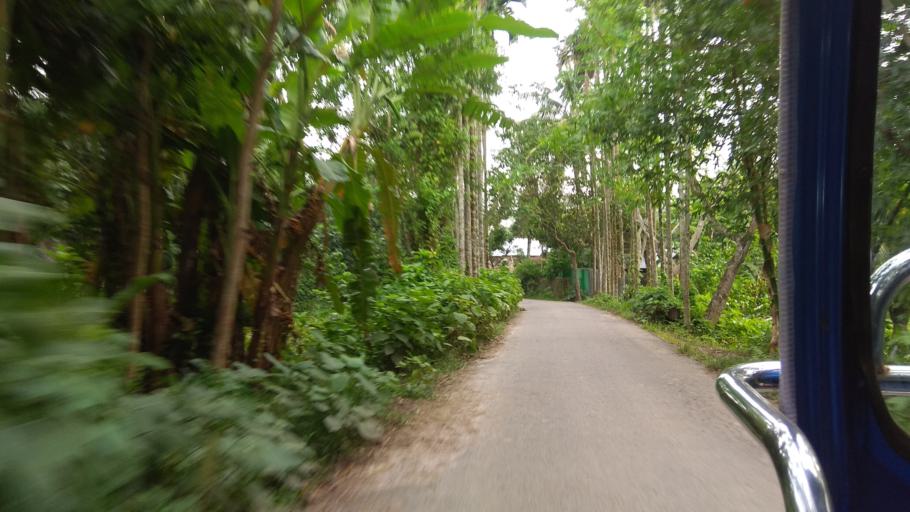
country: BD
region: Khulna
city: Kalia
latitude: 23.0359
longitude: 89.6568
